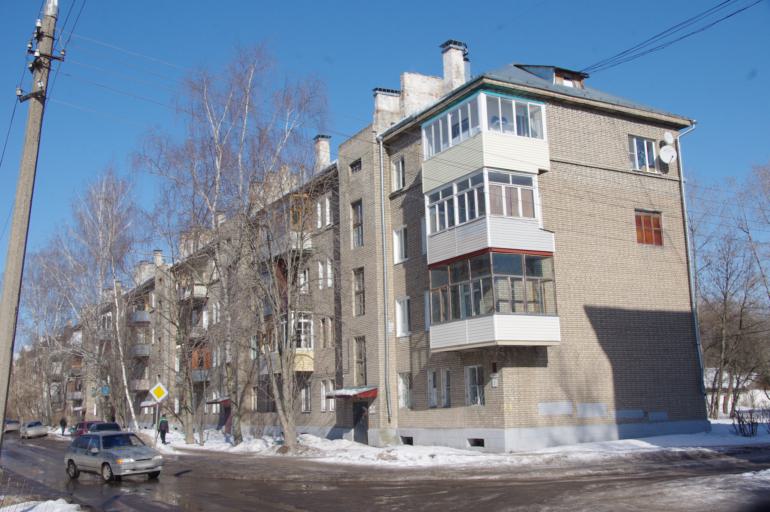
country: RU
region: Moskovskaya
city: Kolomna
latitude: 55.0765
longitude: 38.8046
